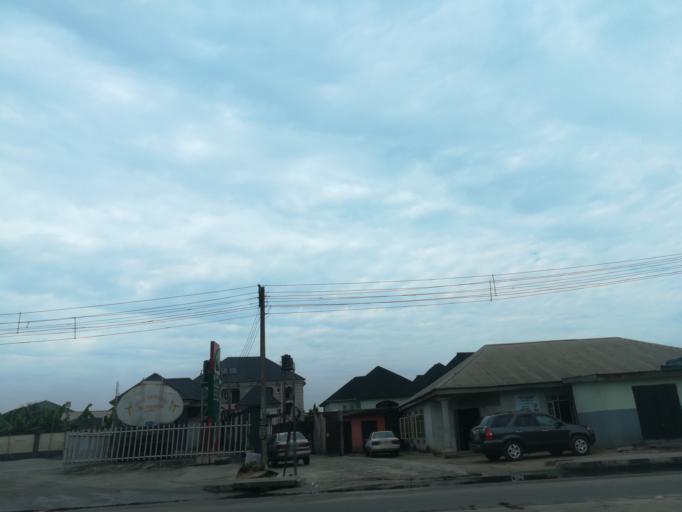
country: NG
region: Rivers
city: Port Harcourt
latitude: 4.8400
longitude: 6.9758
